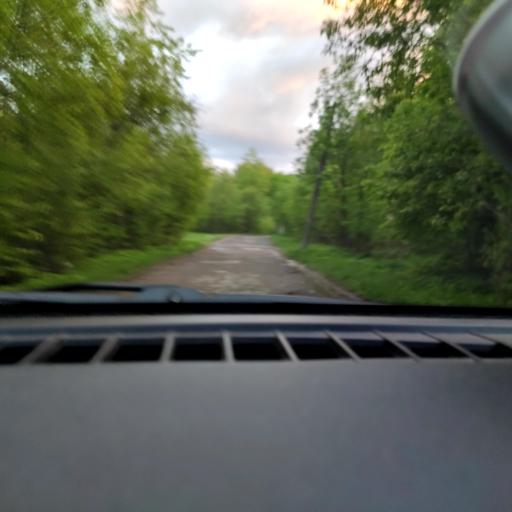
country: RU
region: Perm
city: Perm
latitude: 58.0824
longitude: 56.3845
